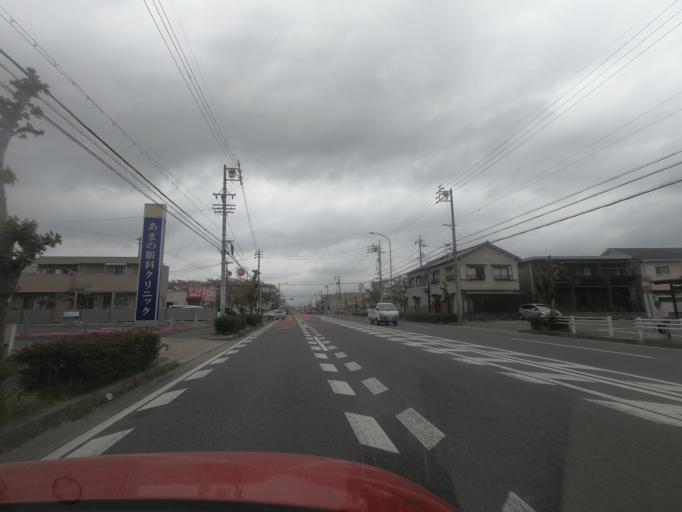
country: JP
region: Aichi
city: Kasugai
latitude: 35.2593
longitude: 136.9672
